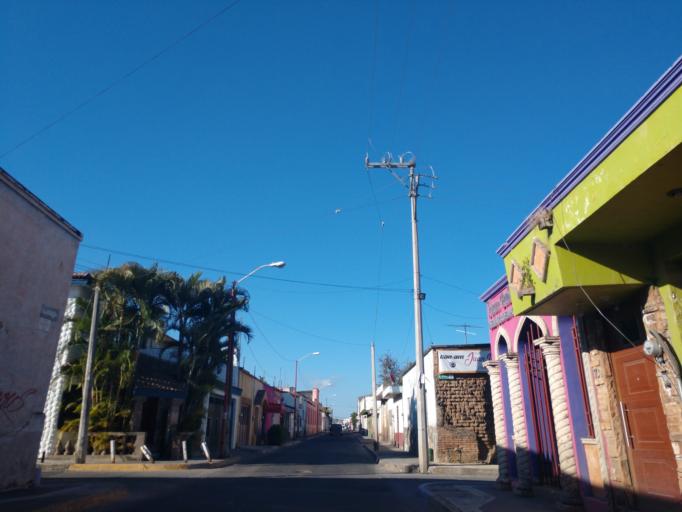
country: MX
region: Nayarit
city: Xalisco
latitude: 21.4426
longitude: -104.8989
